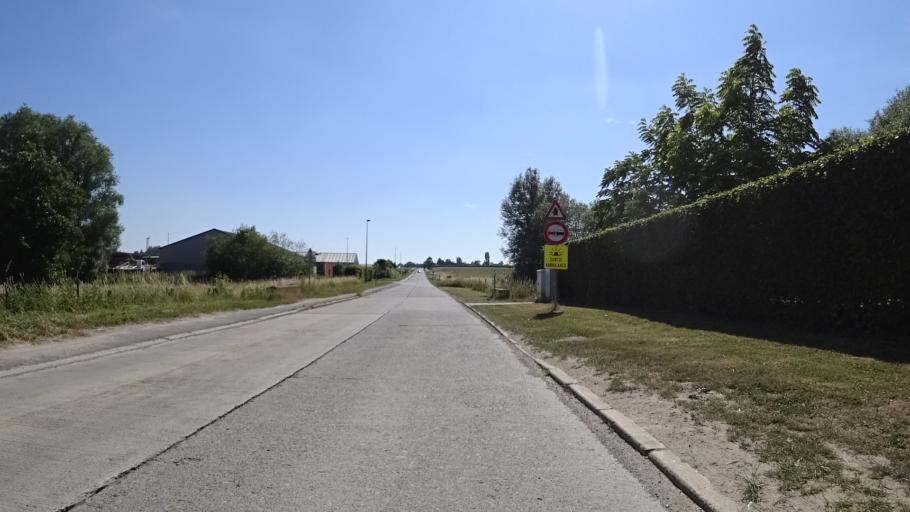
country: BE
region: Wallonia
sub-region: Province du Brabant Wallon
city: Jodoigne
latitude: 50.7186
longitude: 4.8568
